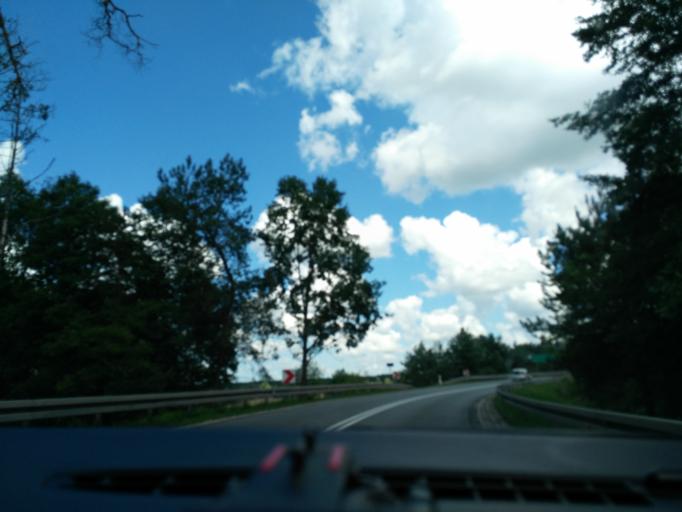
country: PL
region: Masovian Voivodeship
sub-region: Powiat losicki
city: Sarnaki
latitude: 52.3594
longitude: 22.8695
